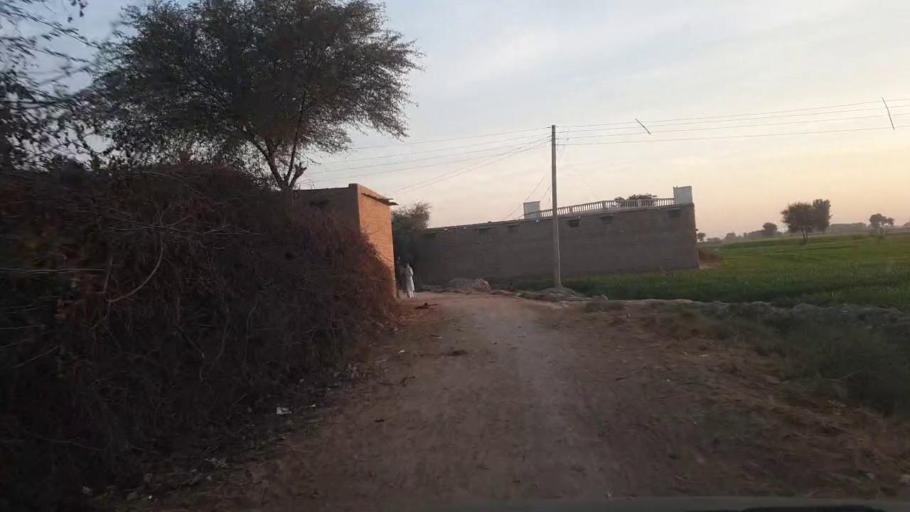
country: PK
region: Sindh
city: Shahpur Chakar
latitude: 26.0757
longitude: 68.5298
